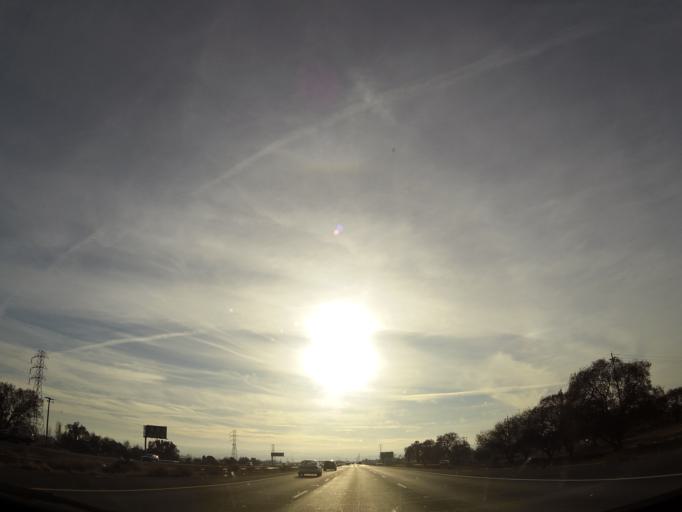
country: US
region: California
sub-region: San Joaquin County
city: Lathrop
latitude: 37.7665
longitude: -121.3331
